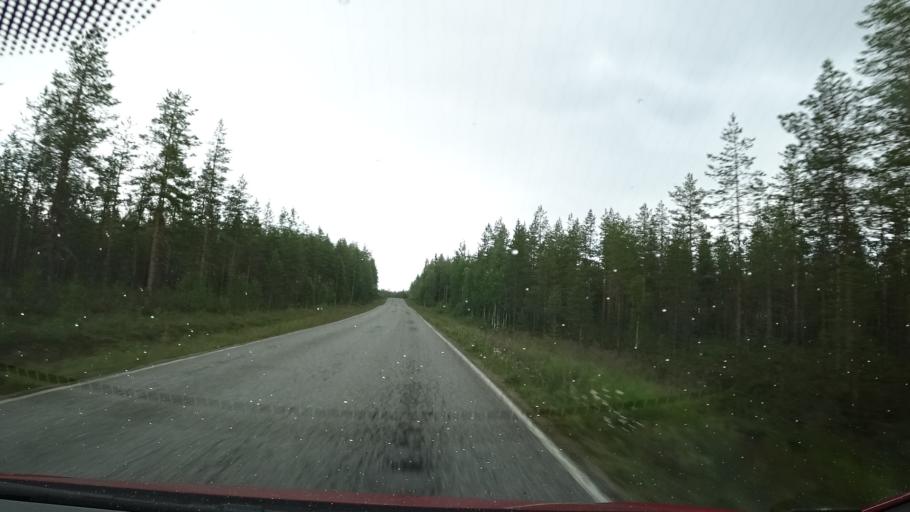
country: FI
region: Kainuu
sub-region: Kehys-Kainuu
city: Kuhmo
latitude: 63.9601
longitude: 29.2634
